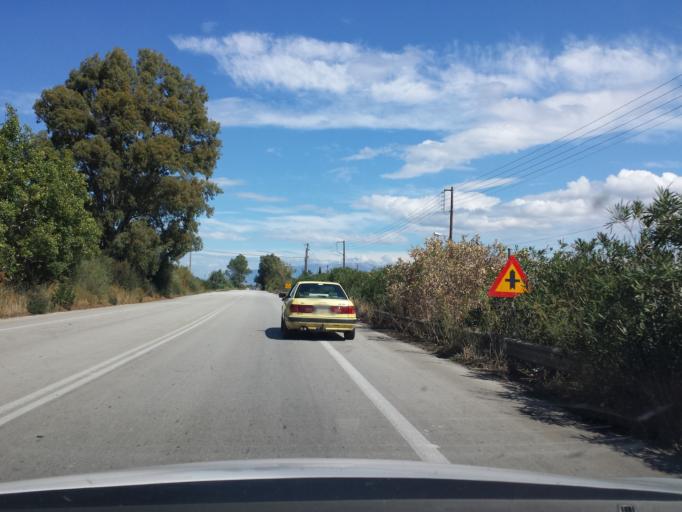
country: GR
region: West Greece
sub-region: Nomos Achaias
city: Limnokhorion
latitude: 38.1051
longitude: 21.4779
